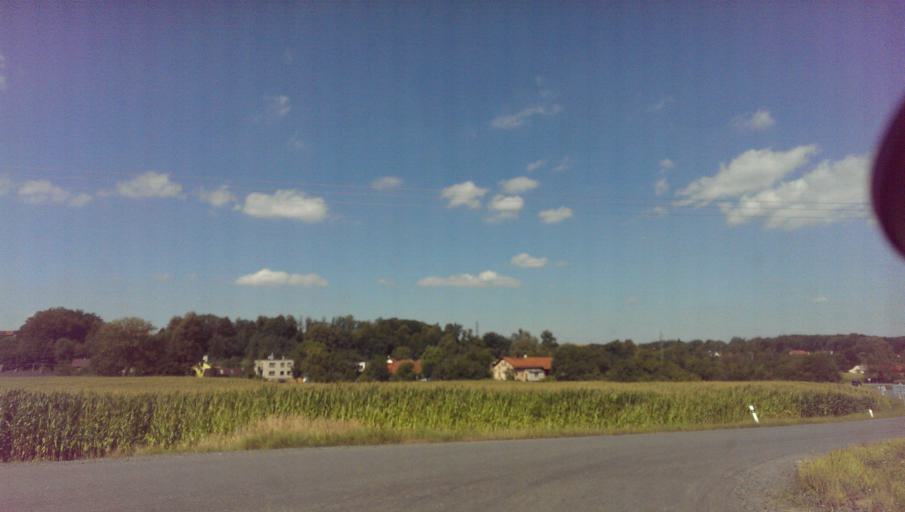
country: CZ
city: Frycovice
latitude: 49.6519
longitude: 18.2214
